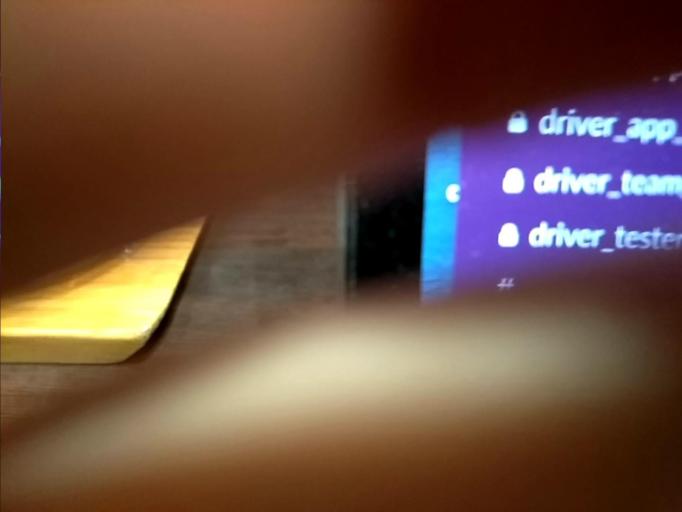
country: RU
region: Moskovskaya
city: Balashikha
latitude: 55.8124
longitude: 37.9654
